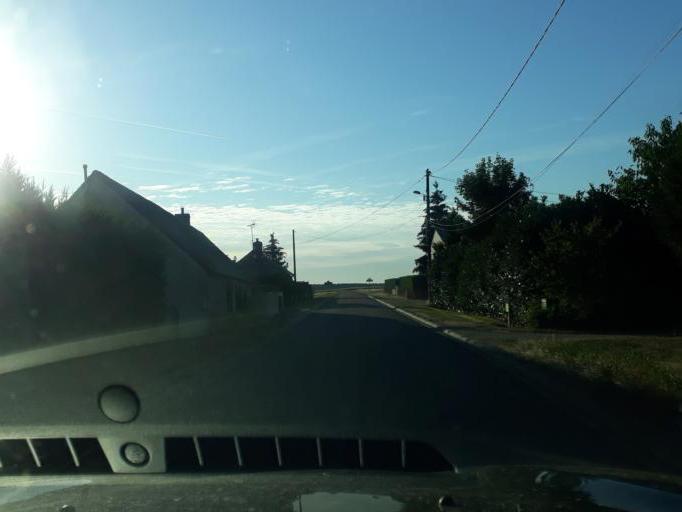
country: FR
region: Centre
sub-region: Departement du Loiret
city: Epieds-en-Beauce
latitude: 47.9419
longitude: 1.5731
